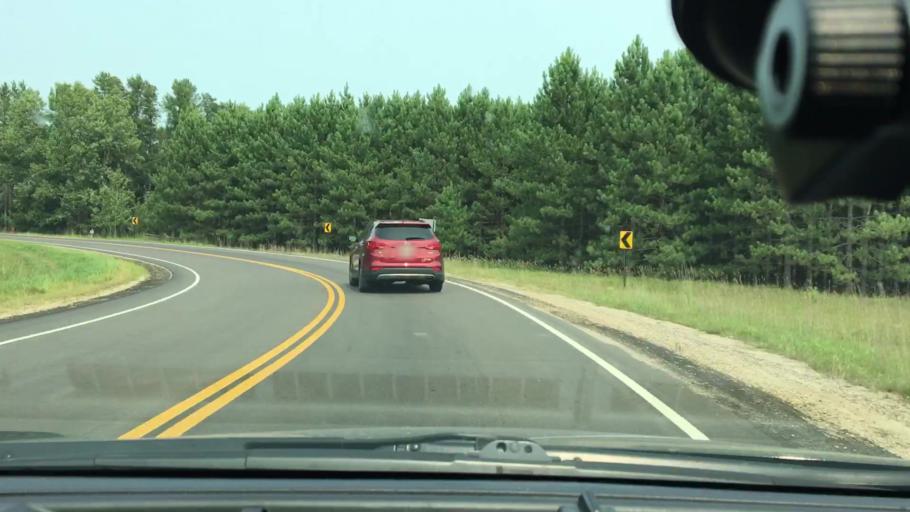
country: US
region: Minnesota
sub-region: Crow Wing County
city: Breezy Point
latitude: 46.5289
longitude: -94.1826
